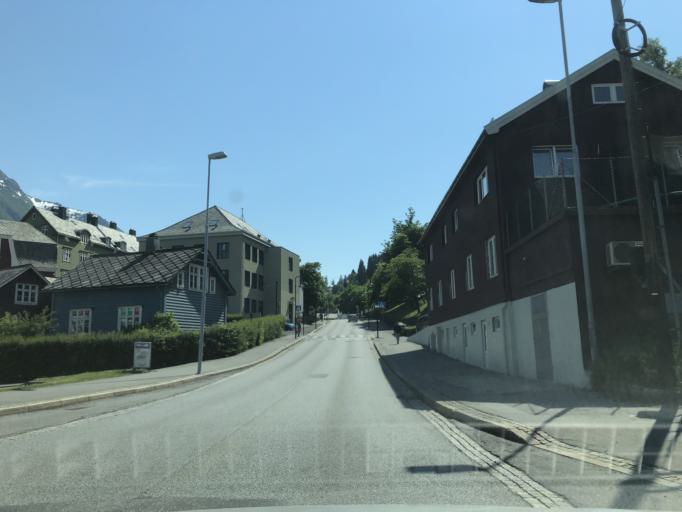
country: NO
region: Hordaland
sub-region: Odda
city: Odda
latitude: 60.0704
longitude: 6.5411
